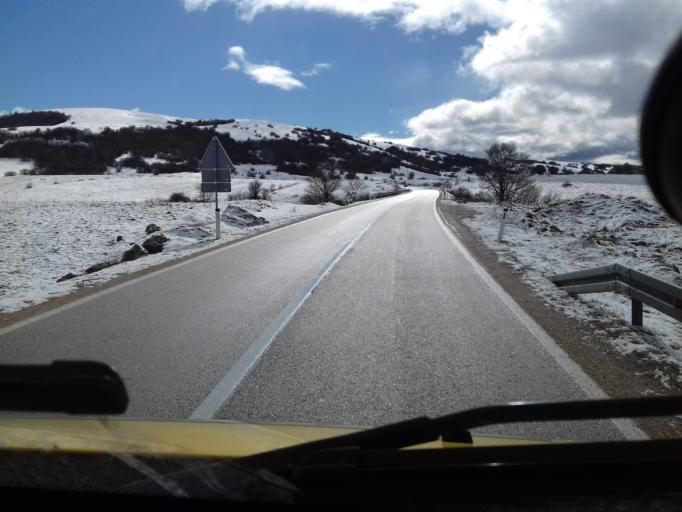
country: BA
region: Federation of Bosnia and Herzegovina
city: Tomislavgrad
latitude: 43.8161
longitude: 17.1990
